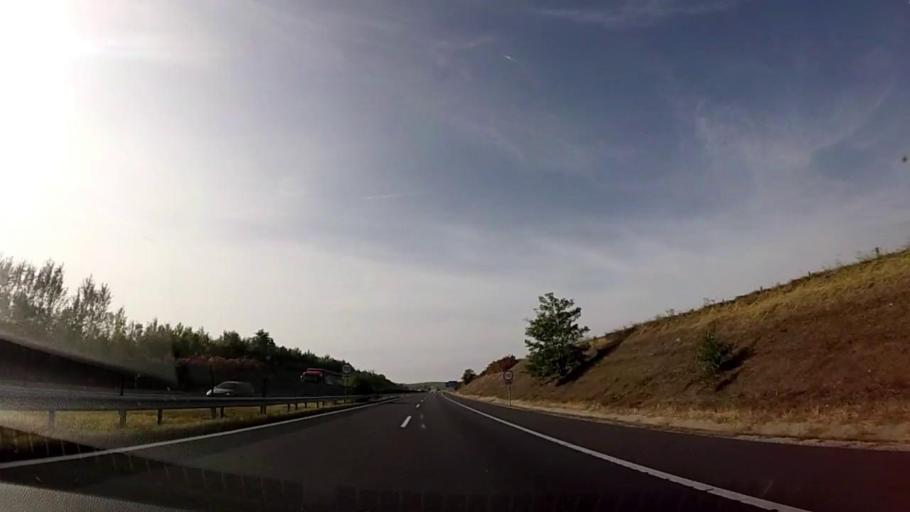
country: HU
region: Somogy
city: Zamardi
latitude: 46.8551
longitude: 17.9612
